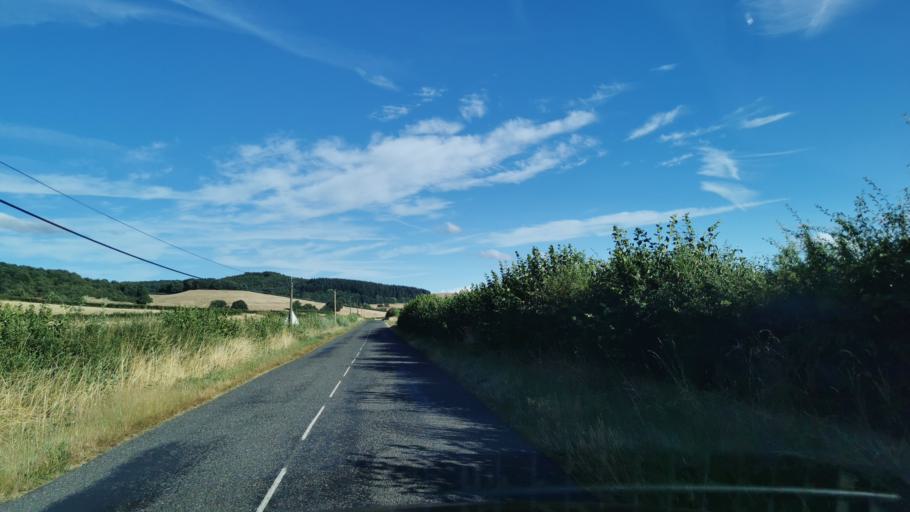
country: FR
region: Bourgogne
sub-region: Departement de Saone-et-Loire
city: Marmagne
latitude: 46.8214
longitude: 4.3240
